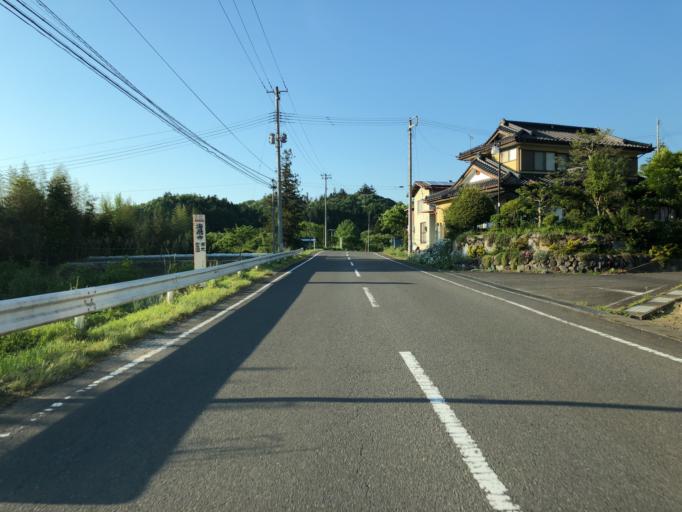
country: JP
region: Fukushima
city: Ishikawa
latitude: 36.9869
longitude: 140.4349
